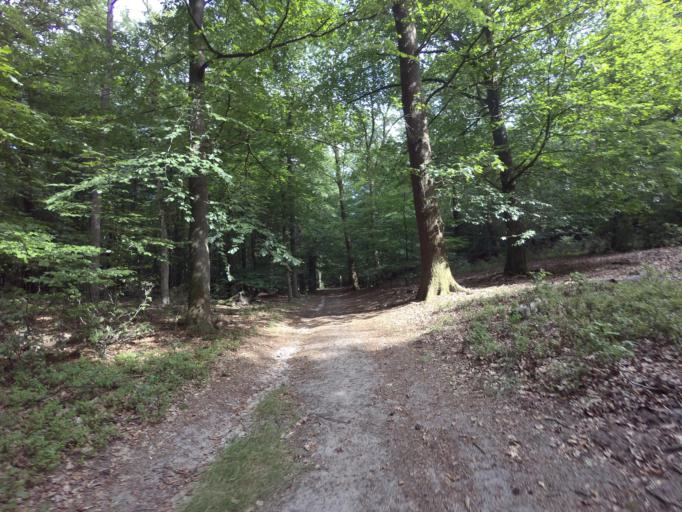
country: NL
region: Gelderland
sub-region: Gemeente Rheden
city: De Steeg
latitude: 52.0532
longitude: 6.0418
